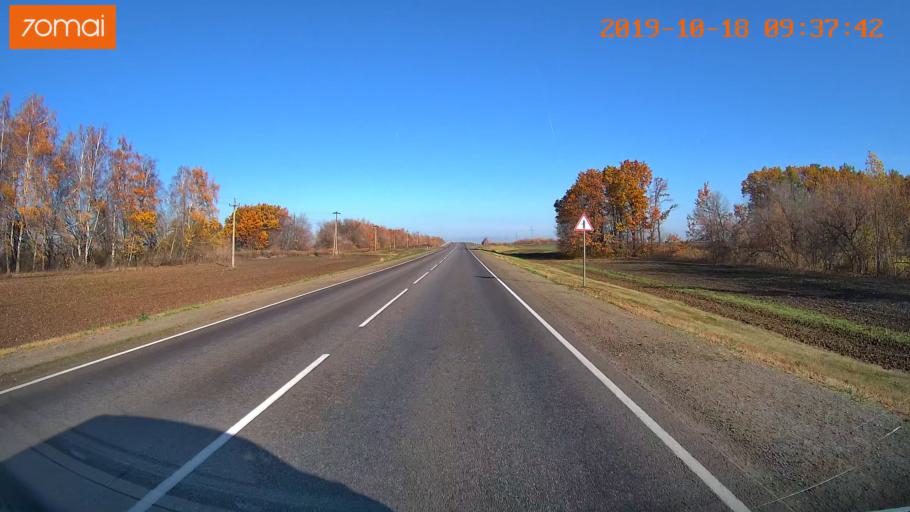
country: RU
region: Tula
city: Yefremov
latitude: 53.2265
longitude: 38.1400
